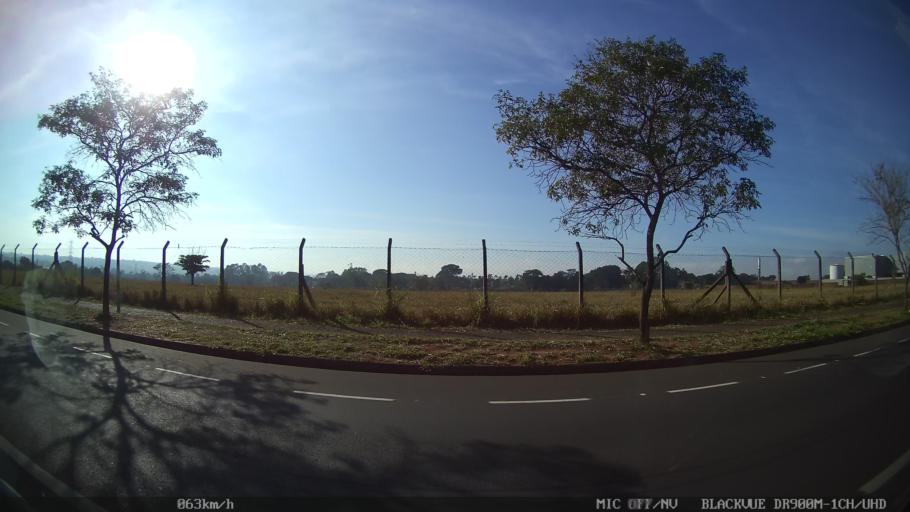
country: BR
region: Sao Paulo
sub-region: Sao Jose Do Rio Preto
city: Sao Jose do Rio Preto
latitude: -20.7974
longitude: -49.3451
